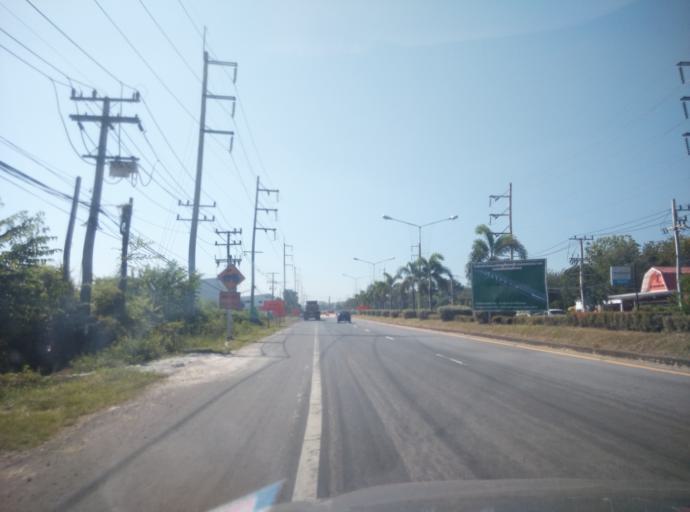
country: TH
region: Sisaket
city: Si Sa Ket
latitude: 15.1259
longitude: 104.2847
